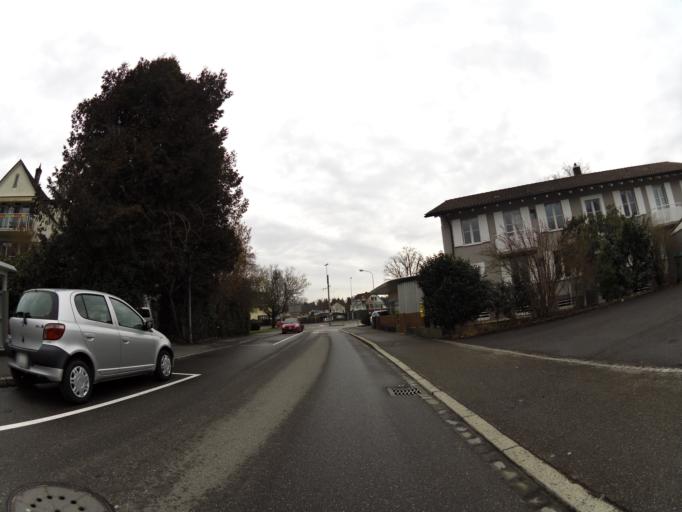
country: CH
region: Aargau
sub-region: Bezirk Aarau
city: Aarau
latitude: 47.3821
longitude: 8.0497
